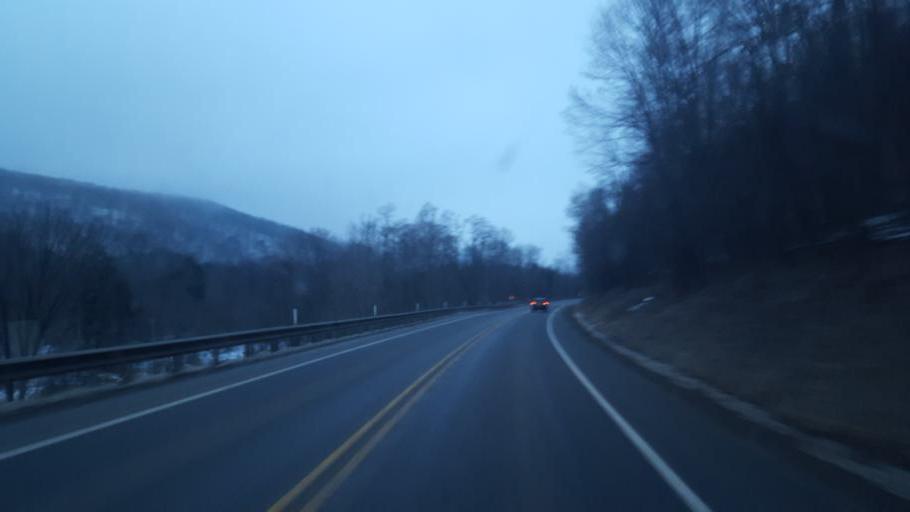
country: US
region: Pennsylvania
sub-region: Potter County
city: Coudersport
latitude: 41.7521
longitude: -78.1036
